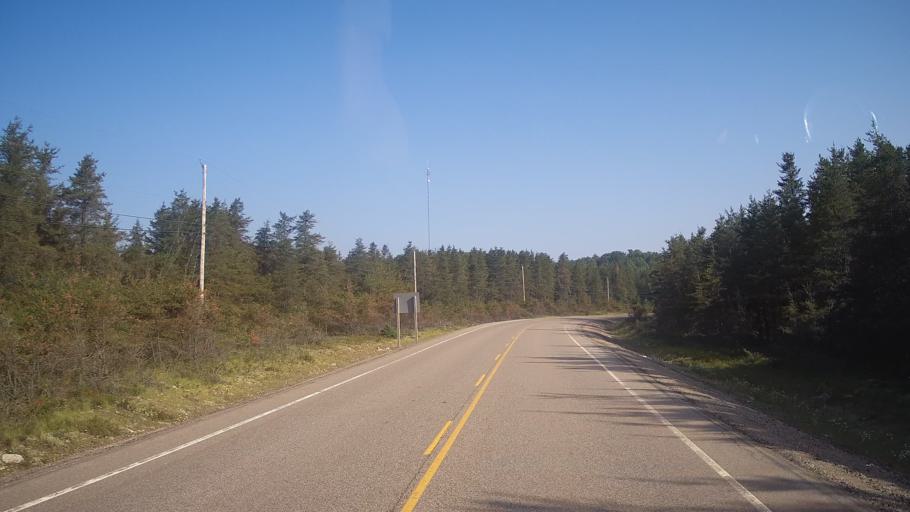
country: CA
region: Ontario
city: Rayside-Balfour
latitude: 46.7068
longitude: -81.5606
